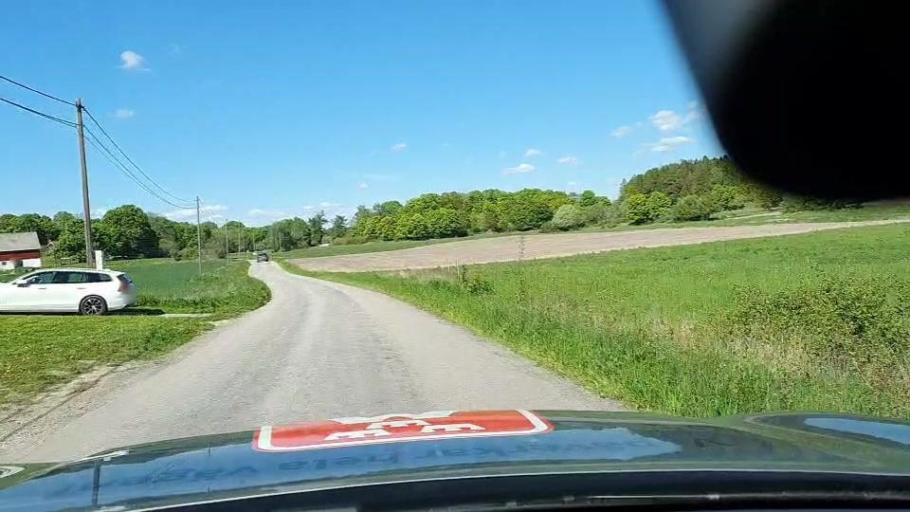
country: SE
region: Soedermanland
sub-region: Strangnas Kommun
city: Strangnas
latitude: 59.4497
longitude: 16.8768
